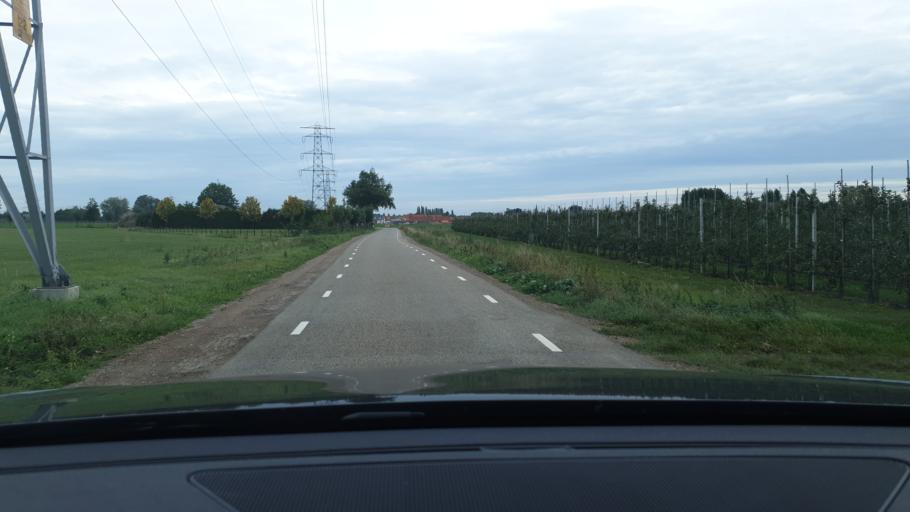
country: NL
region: Gelderland
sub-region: Gemeente Overbetuwe
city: Valburg
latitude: 51.9034
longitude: 5.7941
